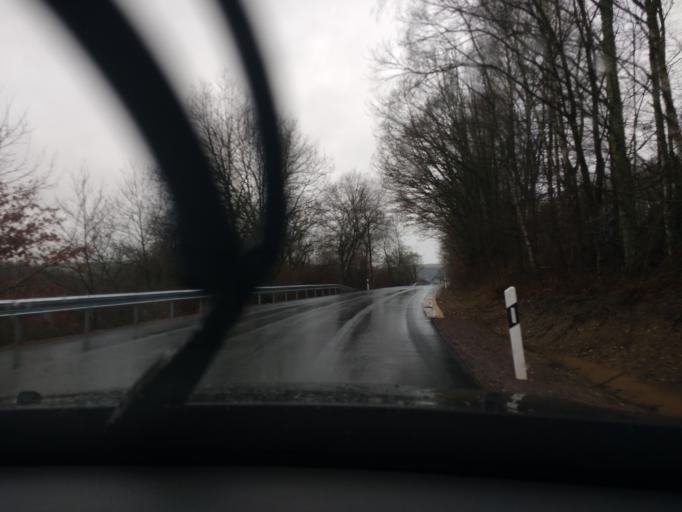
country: DE
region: Rheinland-Pfalz
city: Hinzenburg
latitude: 49.6604
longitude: 6.7312
